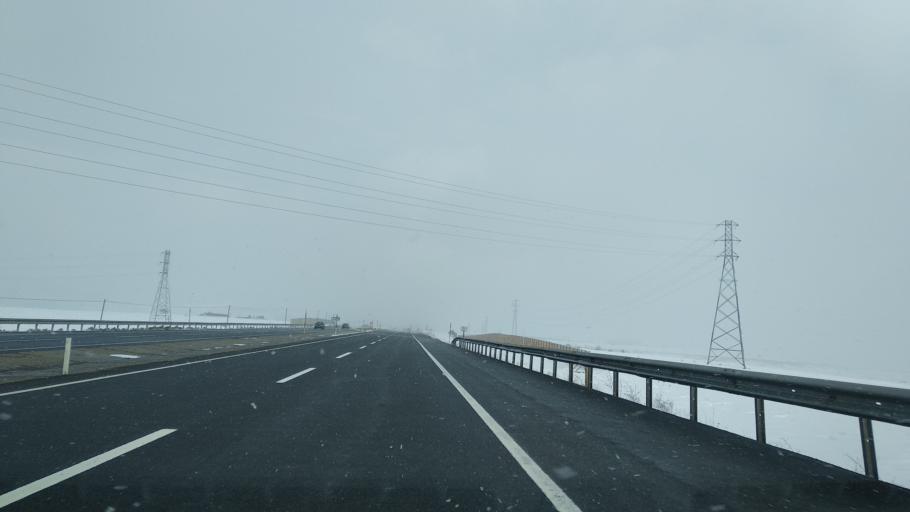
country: TR
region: Kayseri
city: Tomarza
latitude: 38.6269
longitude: 35.7552
